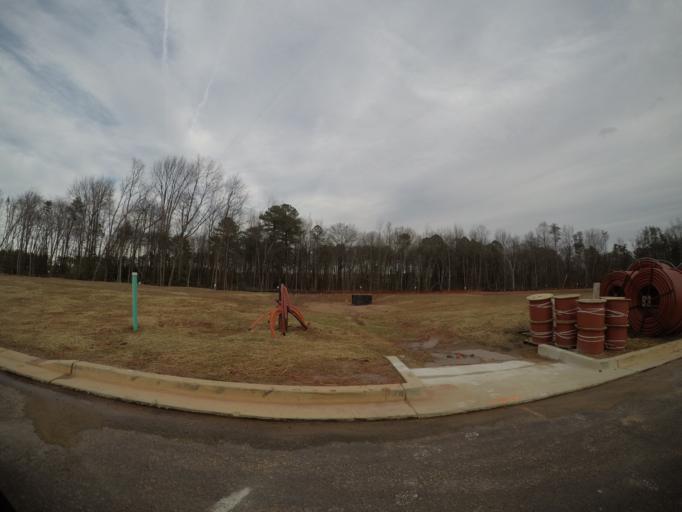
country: US
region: Maryland
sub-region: Anne Arundel County
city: Odenton
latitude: 39.0984
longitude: -76.7050
